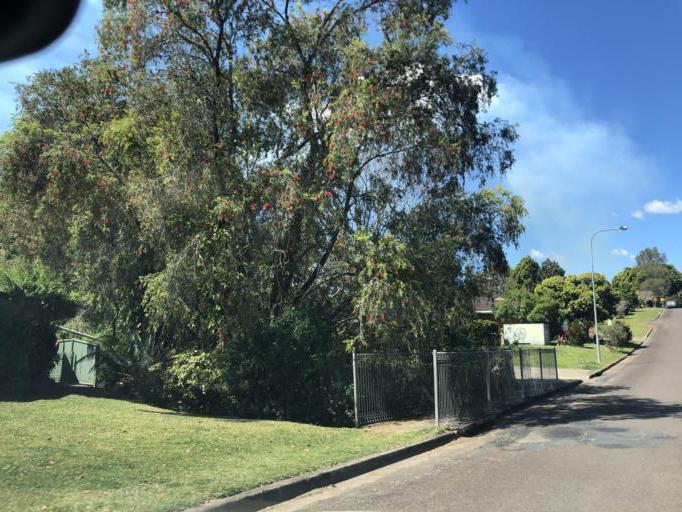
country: AU
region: New South Wales
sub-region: Bellingen
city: Bellingen
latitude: -30.4572
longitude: 152.9025
